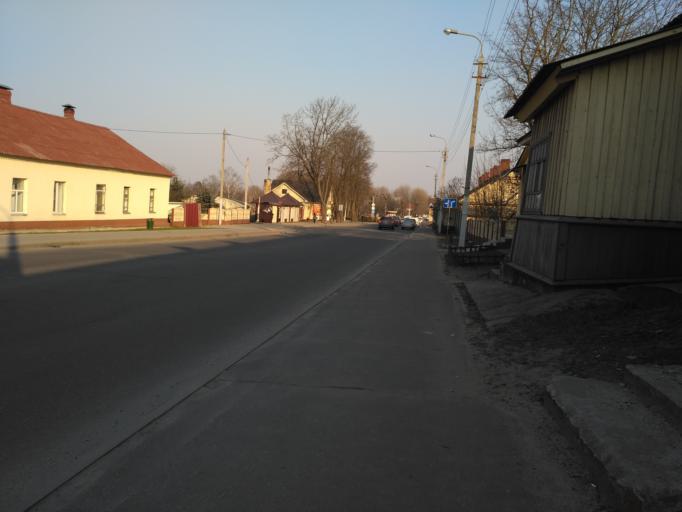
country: BY
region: Minsk
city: Zaslawye
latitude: 54.0072
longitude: 27.2816
